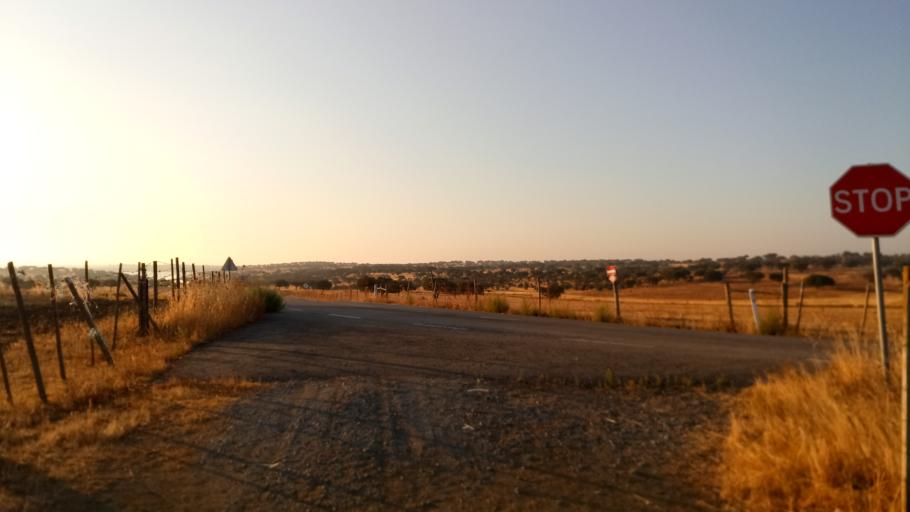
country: PT
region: Evora
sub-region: Reguengos de Monsaraz
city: Reguengos de Monsaraz
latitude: 38.3602
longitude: -7.4588
